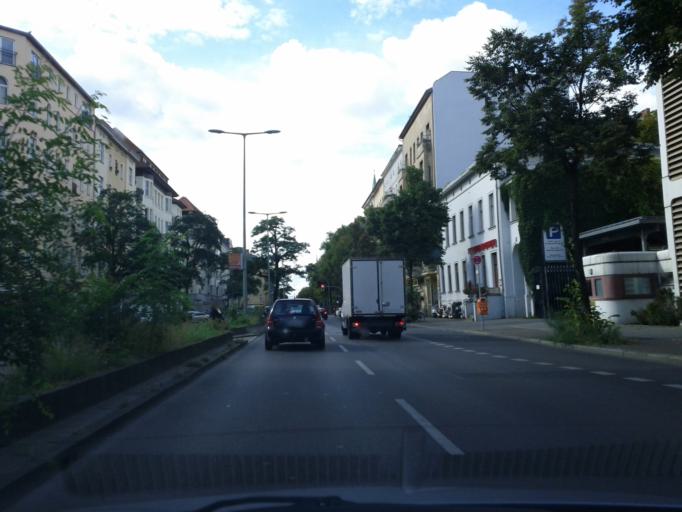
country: DE
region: Berlin
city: Hansaviertel
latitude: 52.5242
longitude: 13.3528
